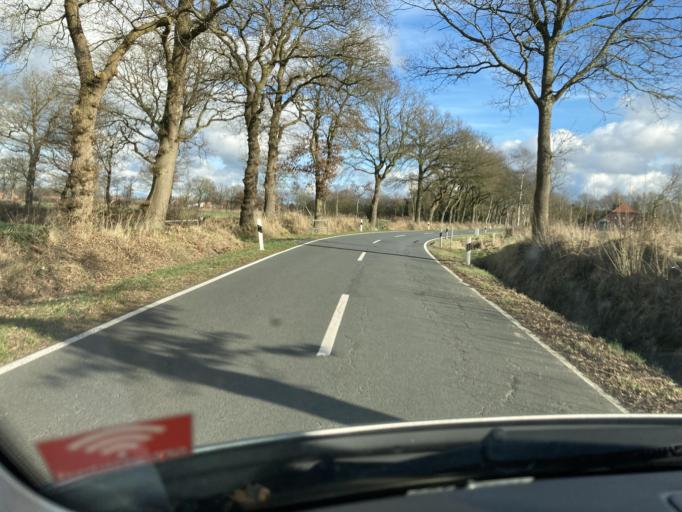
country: DE
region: Lower Saxony
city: Wiesmoor
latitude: 53.3427
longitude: 7.7969
